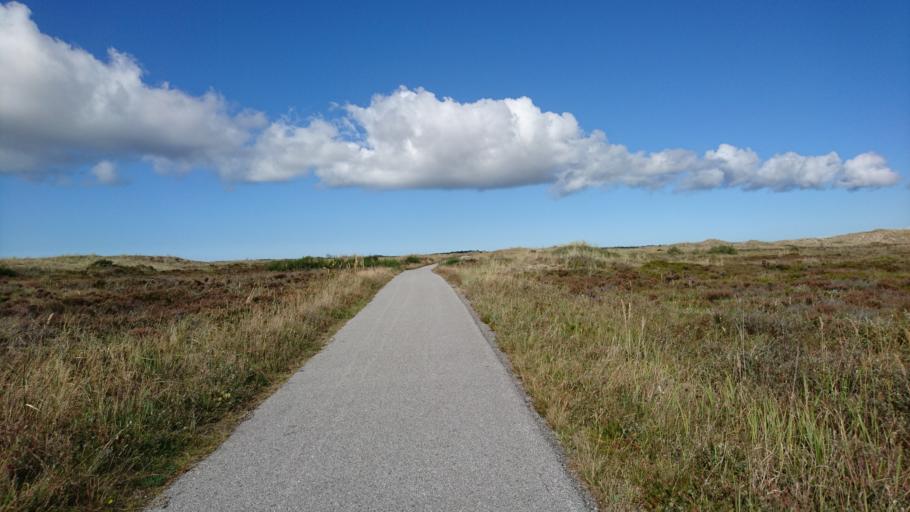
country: DK
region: North Denmark
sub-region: Frederikshavn Kommune
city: Skagen
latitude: 57.6812
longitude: 10.5031
